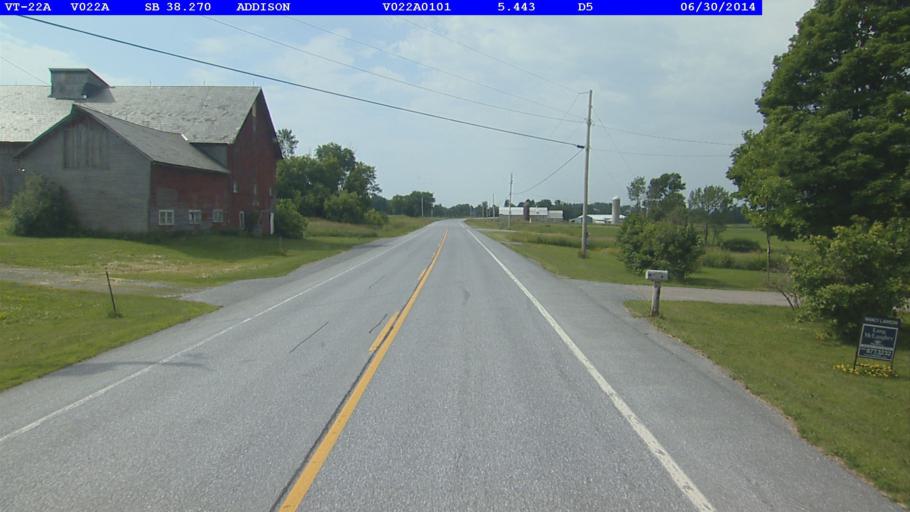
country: US
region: Vermont
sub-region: Addison County
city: Vergennes
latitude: 44.1071
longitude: -73.2954
